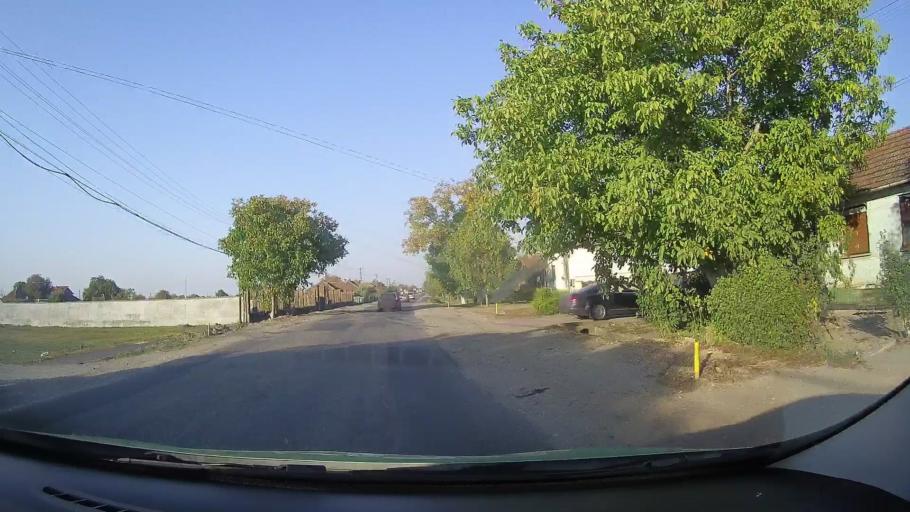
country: RO
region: Arad
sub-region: Comuna Siria
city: Siria
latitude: 46.2764
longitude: 21.6426
